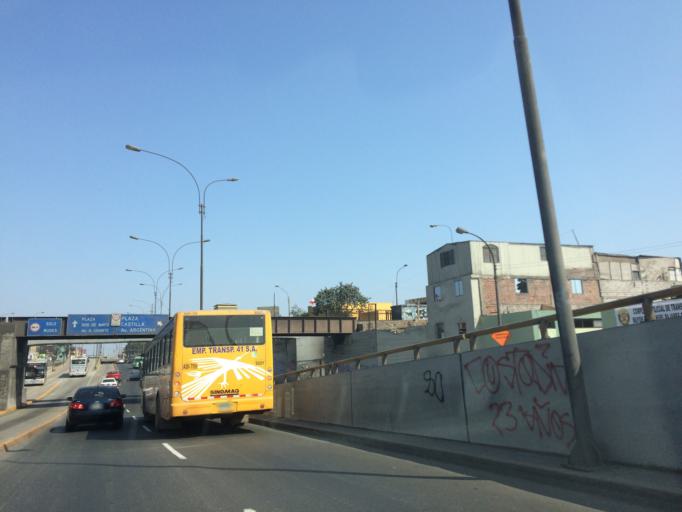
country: PE
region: Lima
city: Lima
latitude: -12.0381
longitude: -77.0435
